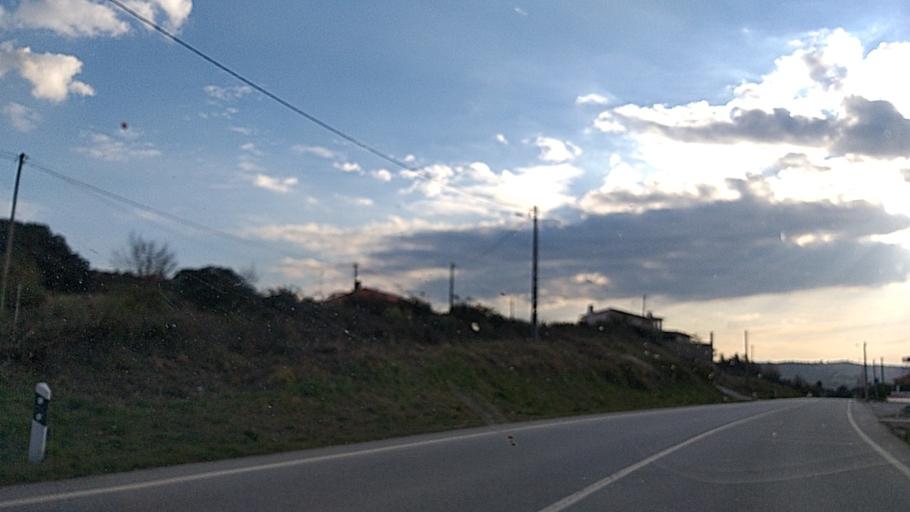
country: ES
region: Castille and Leon
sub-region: Provincia de Salamanca
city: Aldea del Obispo
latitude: 40.7145
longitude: -6.9088
